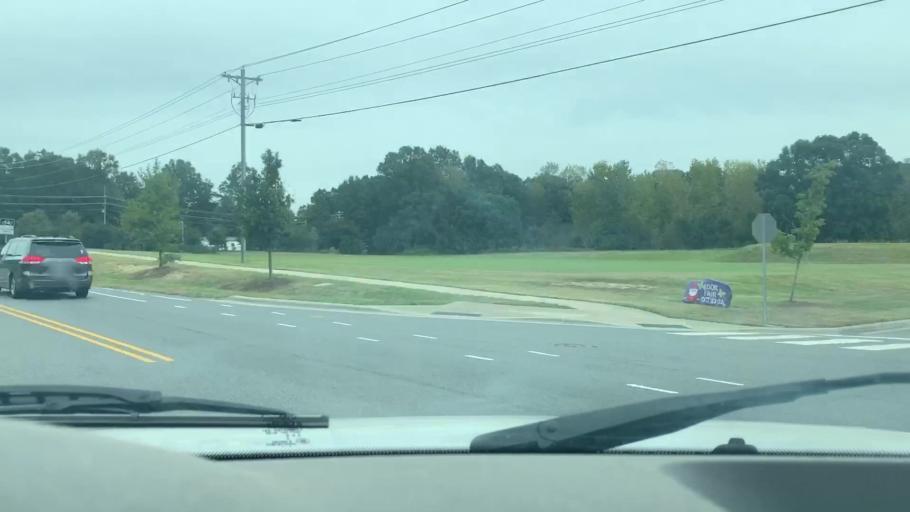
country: US
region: North Carolina
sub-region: Mecklenburg County
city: Huntersville
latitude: 35.4275
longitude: -80.8733
